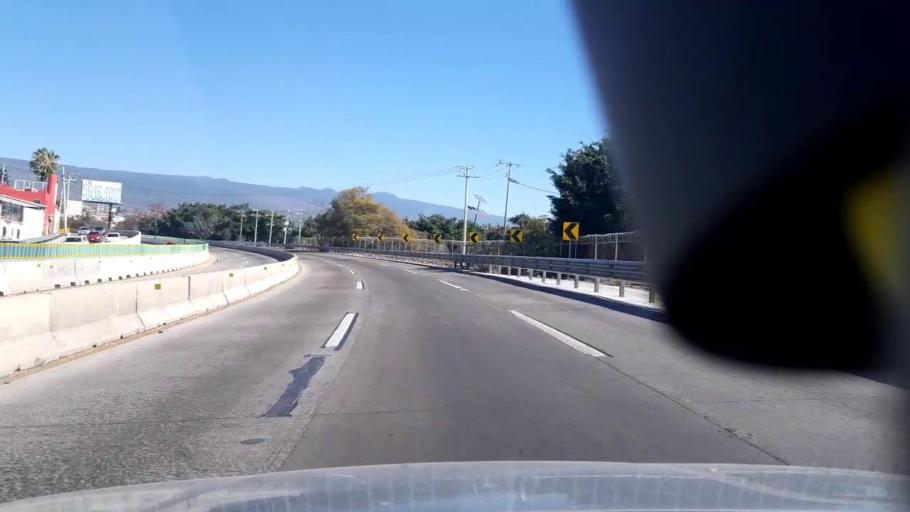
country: MX
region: Morelos
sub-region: Cuernavaca
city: Colonia los Cerritos
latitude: 18.9386
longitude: -99.1903
